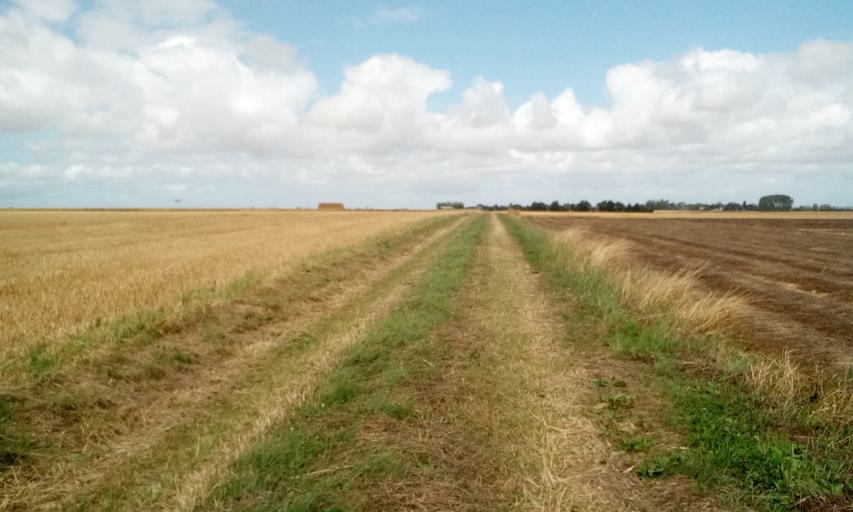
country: FR
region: Lower Normandy
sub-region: Departement du Calvados
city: Cheux
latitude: 49.1772
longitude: -0.5548
